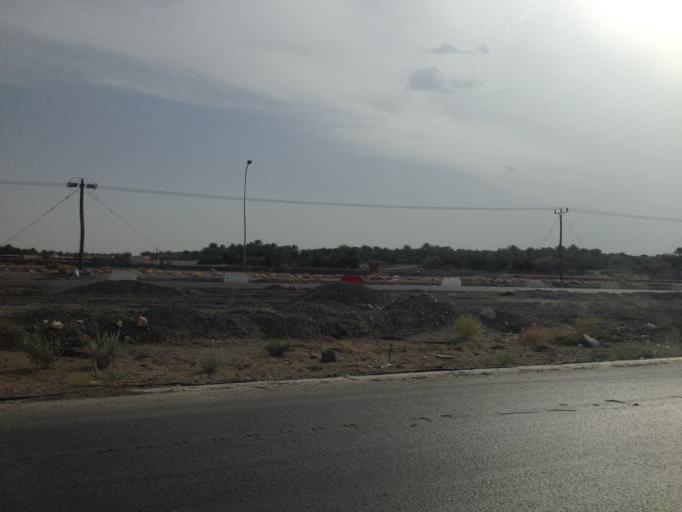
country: OM
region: Ash Sharqiyah
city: Al Qabil
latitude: 22.5678
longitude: 58.7013
